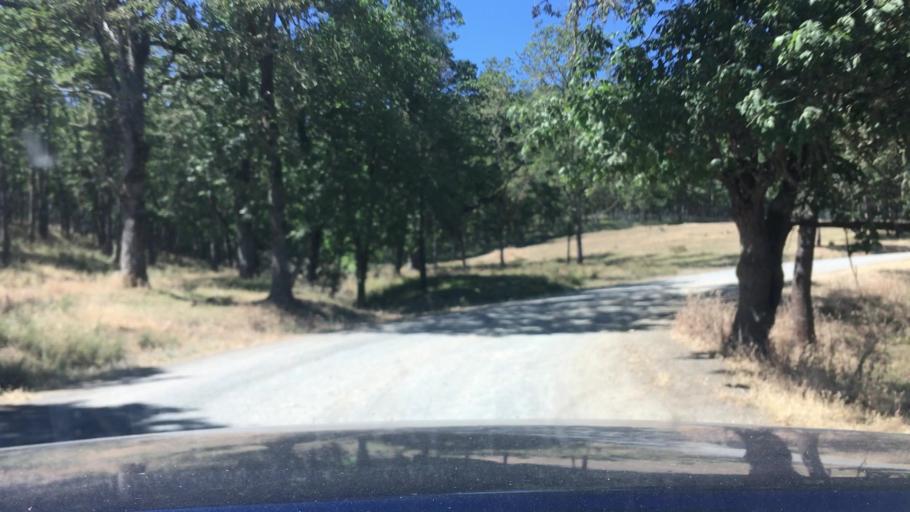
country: US
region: Oregon
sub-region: Douglas County
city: Winston
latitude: 43.1386
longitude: -123.4414
